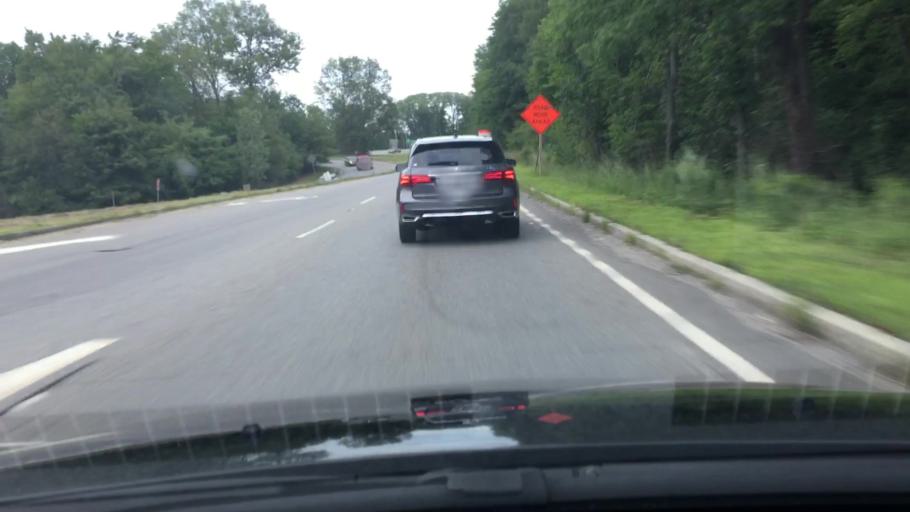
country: US
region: Massachusetts
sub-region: Worcester County
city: Shrewsbury
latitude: 42.2813
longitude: -71.6703
